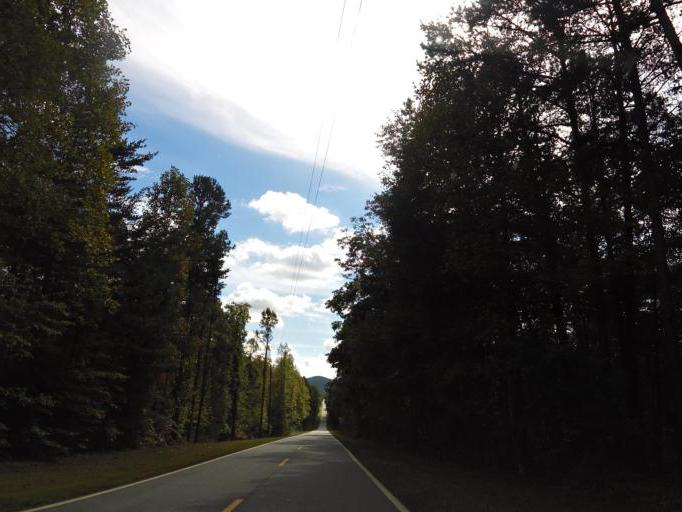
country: US
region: Georgia
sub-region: Pickens County
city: Nelson
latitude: 34.4725
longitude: -84.2588
